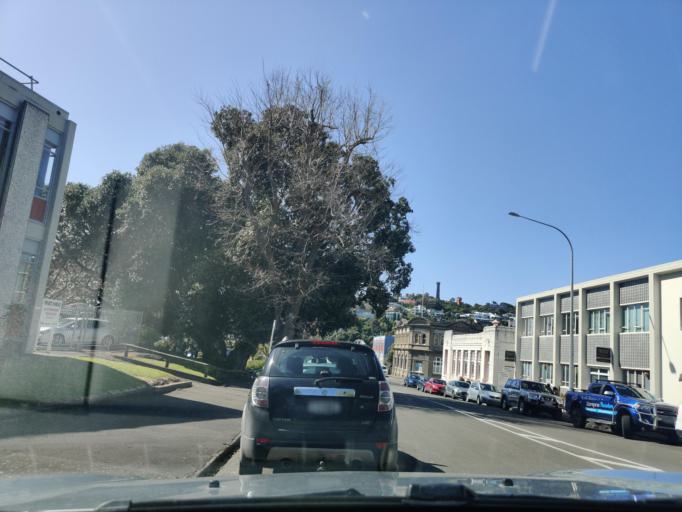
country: NZ
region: Manawatu-Wanganui
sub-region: Wanganui District
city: Wanganui
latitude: -39.9319
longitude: 175.0561
